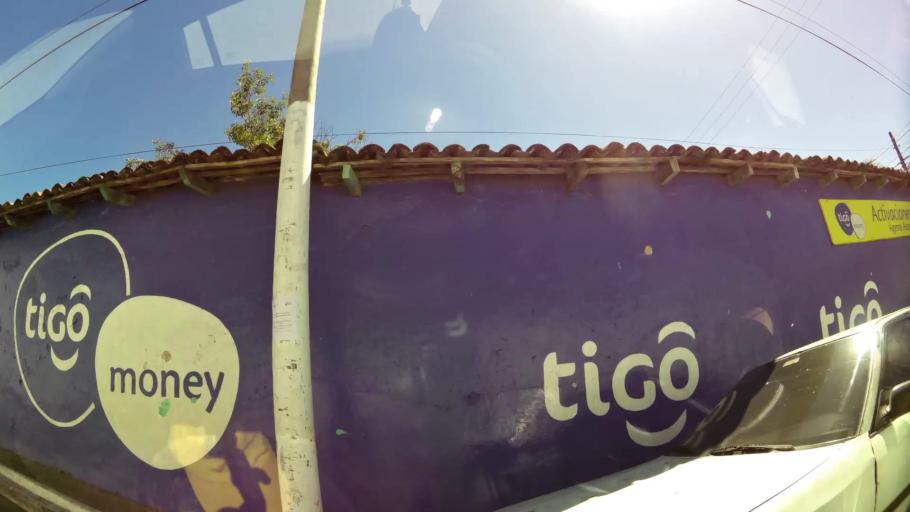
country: SV
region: La Libertad
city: San Juan Opico
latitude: 13.8759
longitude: -89.3577
